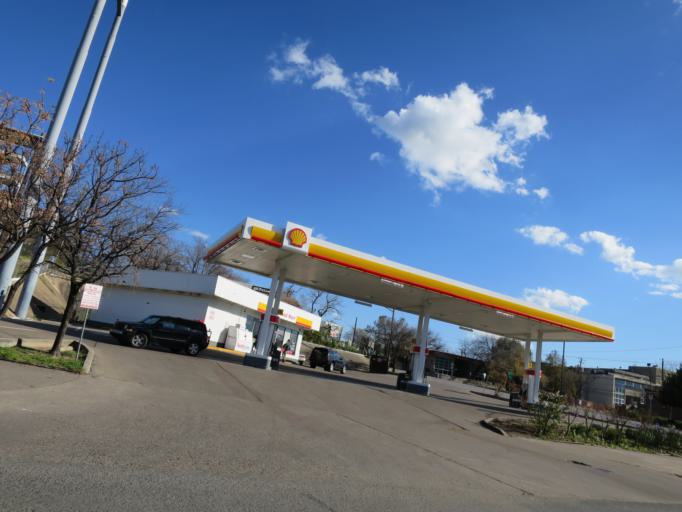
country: US
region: Texas
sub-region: Travis County
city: Austin
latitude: 30.2670
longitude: -97.7337
